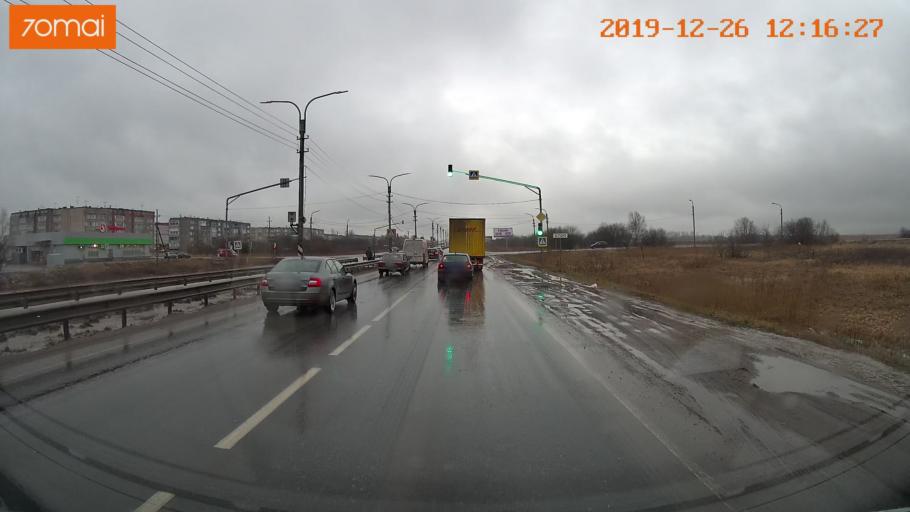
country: RU
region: Vologda
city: Tonshalovo
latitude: 59.1977
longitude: 37.9425
